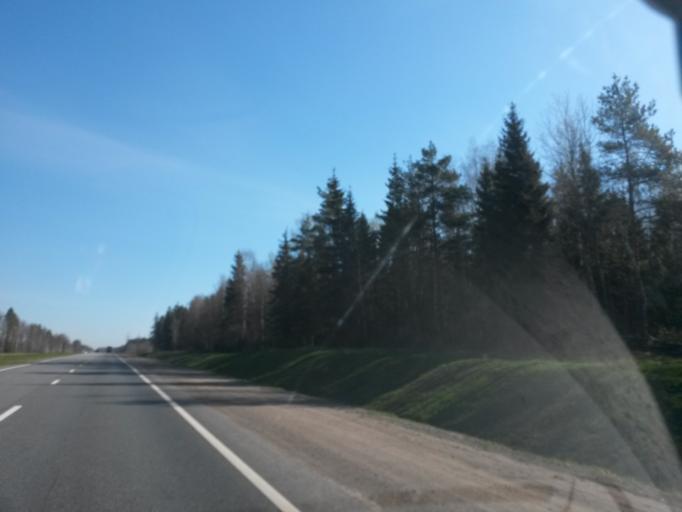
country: RU
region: Jaroslavl
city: Krasnyye Tkachi
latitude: 57.4723
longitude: 39.7602
